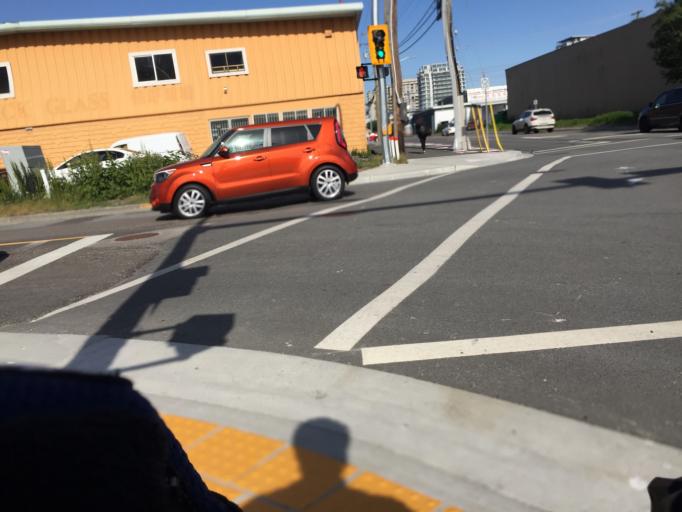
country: CA
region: British Columbia
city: Richmond
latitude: 49.1740
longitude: -123.1425
